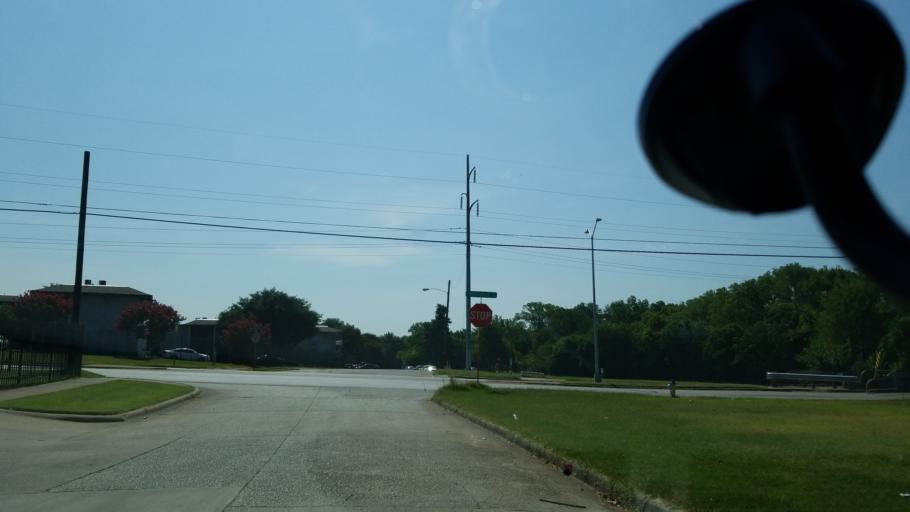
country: US
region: Texas
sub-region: Dallas County
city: Cockrell Hill
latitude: 32.7070
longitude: -96.8749
